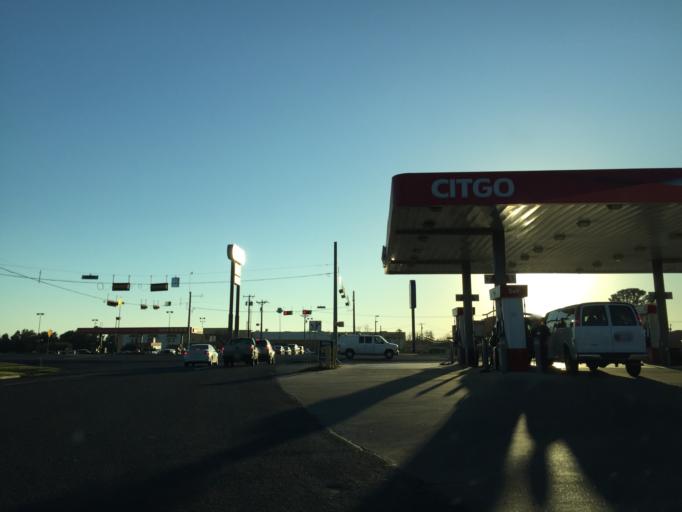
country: US
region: Texas
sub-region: Bastrop County
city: Elgin
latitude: 30.3479
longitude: -97.3826
